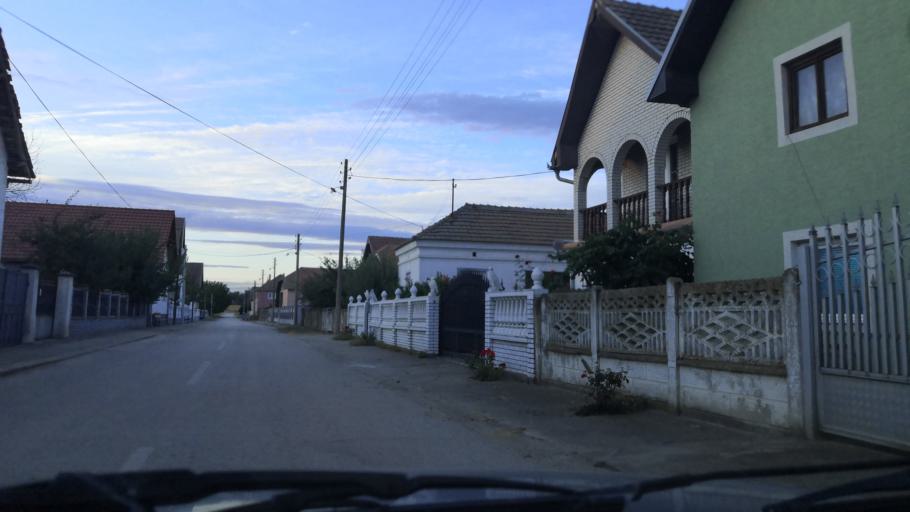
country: RO
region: Mehedinti
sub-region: Comuna Gruia
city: Gruia
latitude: 44.2686
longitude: 22.6678
